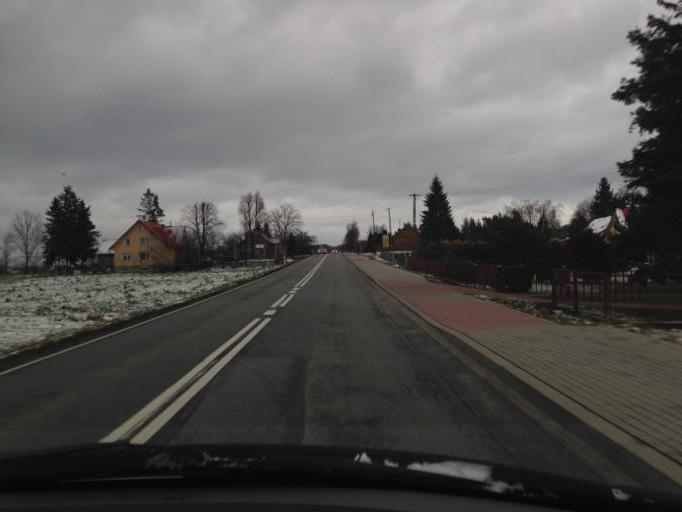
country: PL
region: Lesser Poland Voivodeship
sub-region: Powiat tarnowski
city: Zakliczyn
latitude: 49.8528
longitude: 20.8278
